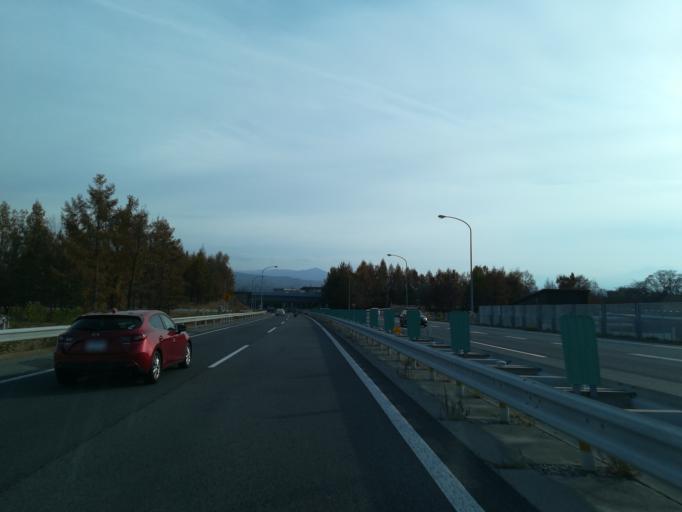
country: JP
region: Nagano
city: Komoro
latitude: 36.2890
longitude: 138.4829
